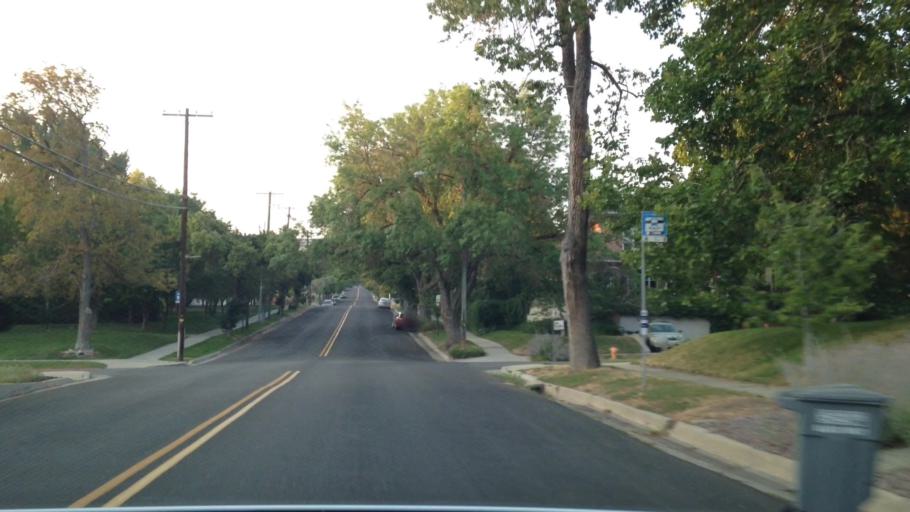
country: US
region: Utah
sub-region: Salt Lake County
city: Salt Lake City
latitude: 40.7781
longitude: -111.8775
